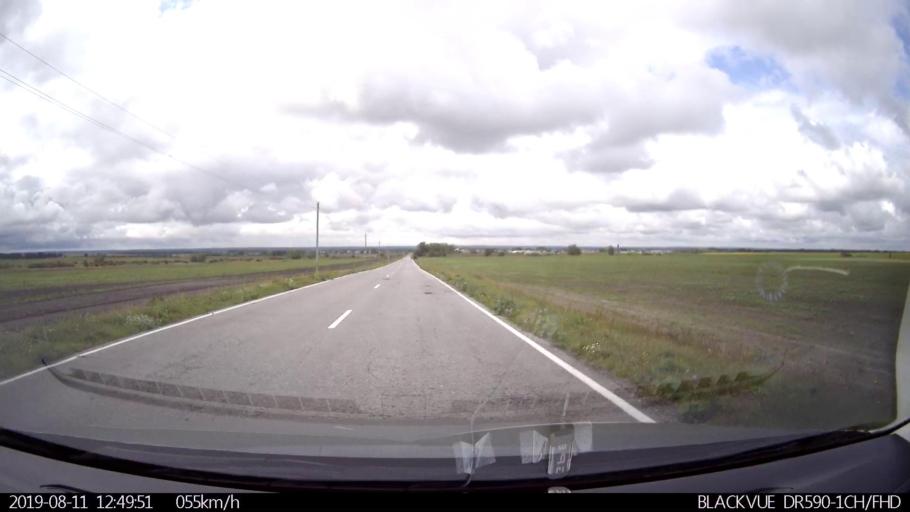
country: RU
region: Ulyanovsk
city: Ignatovka
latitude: 53.8758
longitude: 47.6806
